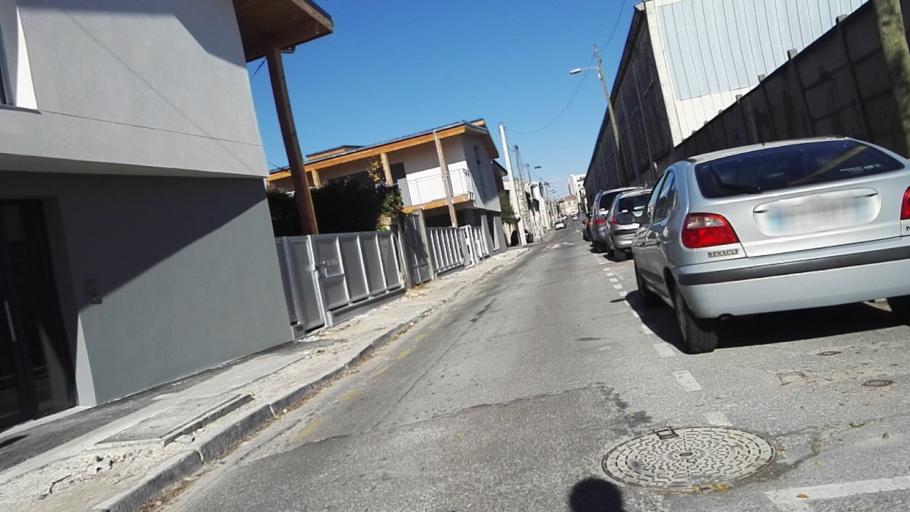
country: FR
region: Aquitaine
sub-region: Departement de la Gironde
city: Bordeaux
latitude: 44.8335
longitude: -0.6018
